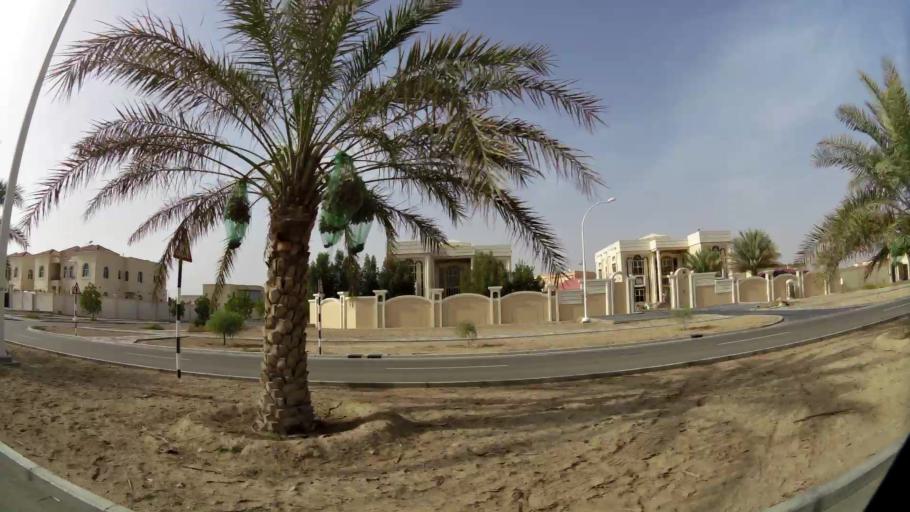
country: AE
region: Abu Dhabi
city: Al Ain
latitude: 24.1530
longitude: 55.7161
